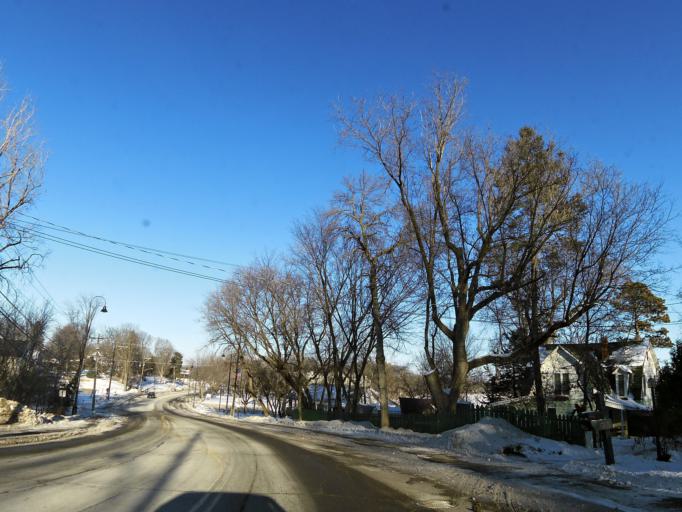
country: US
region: Minnesota
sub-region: Hennepin County
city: Mound
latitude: 44.9277
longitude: -93.6721
